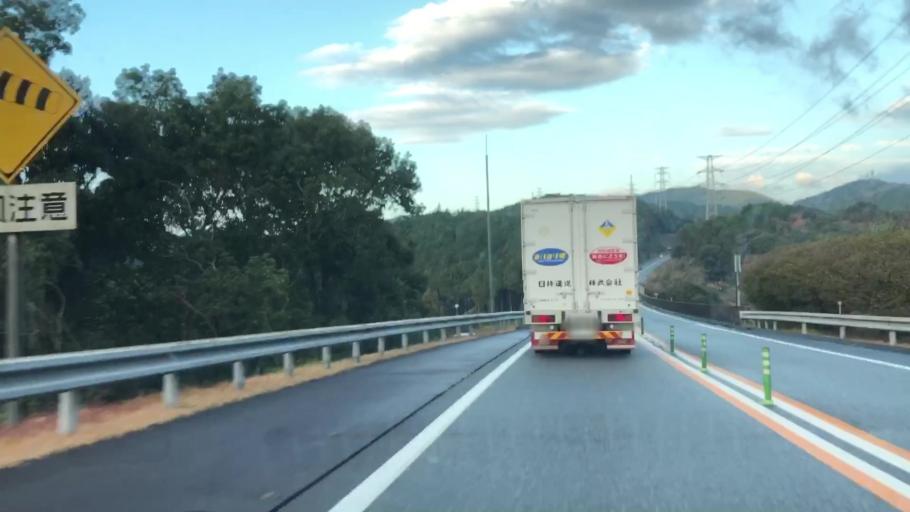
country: JP
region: Saga Prefecture
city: Imaricho-ko
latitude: 33.1549
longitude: 129.8805
